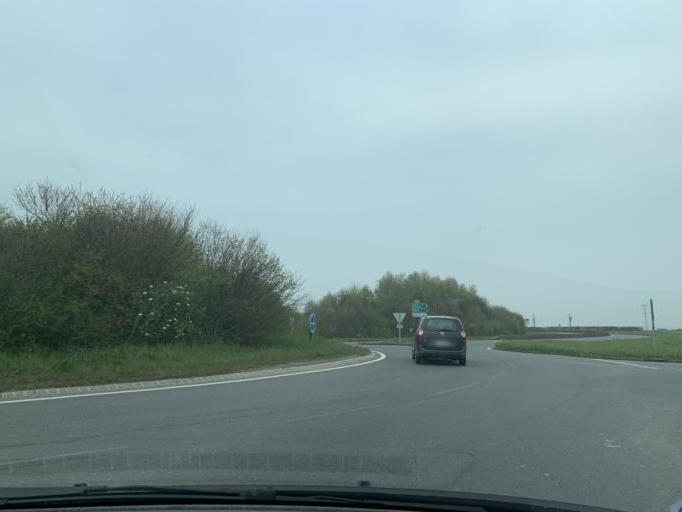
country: FR
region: Nord-Pas-de-Calais
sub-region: Departement du Pas-de-Calais
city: Montreuil
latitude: 50.4331
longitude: 1.7359
